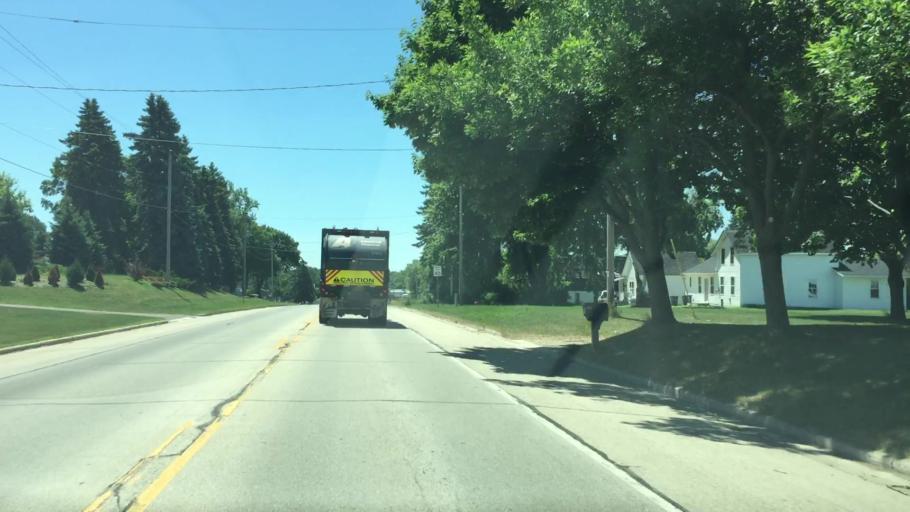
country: US
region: Wisconsin
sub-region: Calumet County
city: Chilton
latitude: 44.0422
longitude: -88.1630
